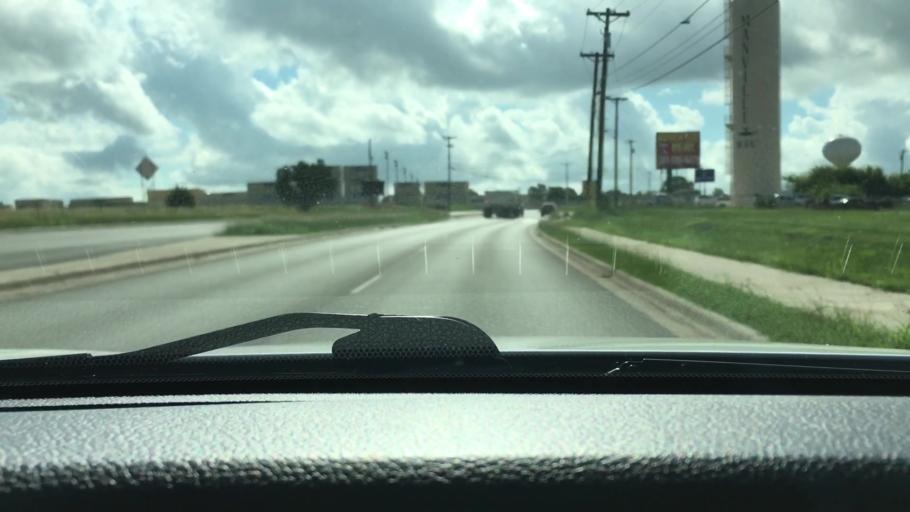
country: US
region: Texas
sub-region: Travis County
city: Windemere
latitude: 30.4821
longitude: -97.6466
